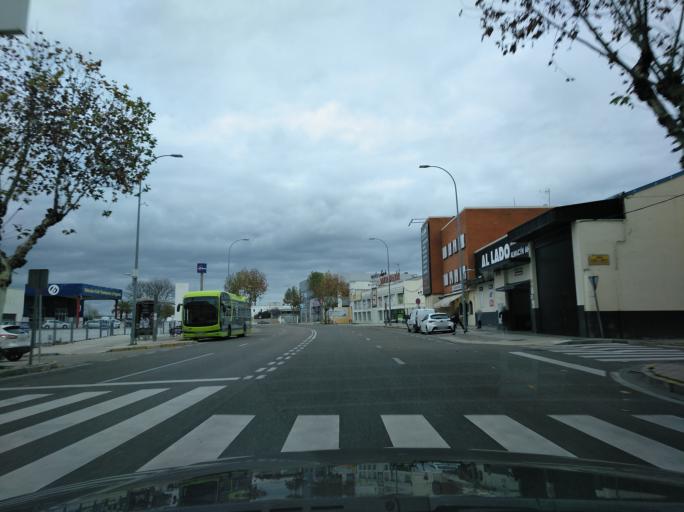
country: ES
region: Extremadura
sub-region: Provincia de Badajoz
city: Badajoz
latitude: 38.8785
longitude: -6.9510
